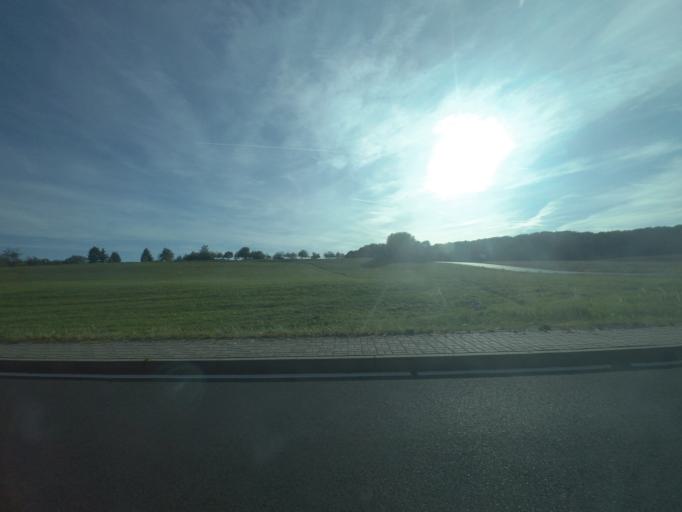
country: DE
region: Hesse
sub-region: Regierungsbezirk Kassel
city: Neuhof
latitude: 50.4577
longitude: 9.5969
